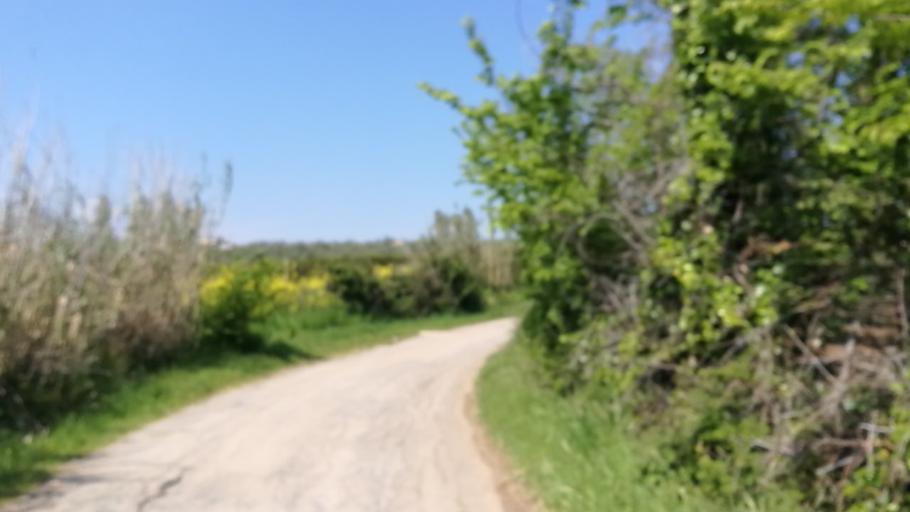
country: IT
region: Molise
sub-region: Provincia di Campobasso
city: Termoli
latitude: 41.9715
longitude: 14.9865
